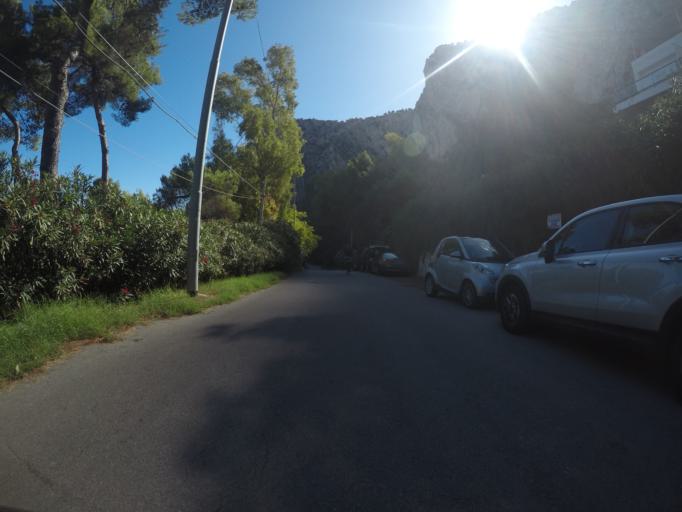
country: IT
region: Sicily
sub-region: Palermo
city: Palermo
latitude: 38.1870
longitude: 13.3454
